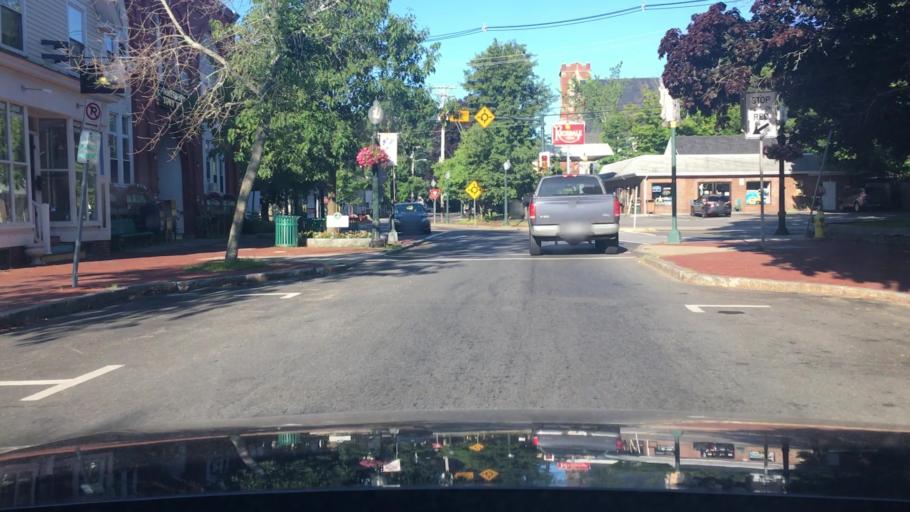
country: US
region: Massachusetts
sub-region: Essex County
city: Amesbury
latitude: 42.8566
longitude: -70.9331
